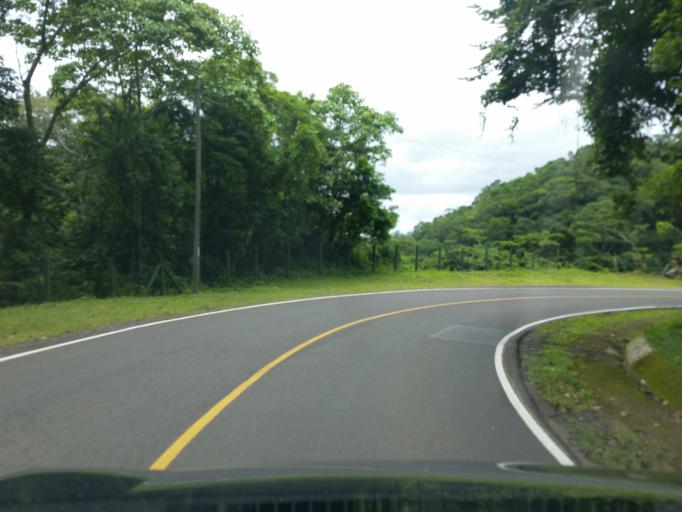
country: NI
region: Matagalpa
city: San Ramon
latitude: 12.9601
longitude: -85.8619
